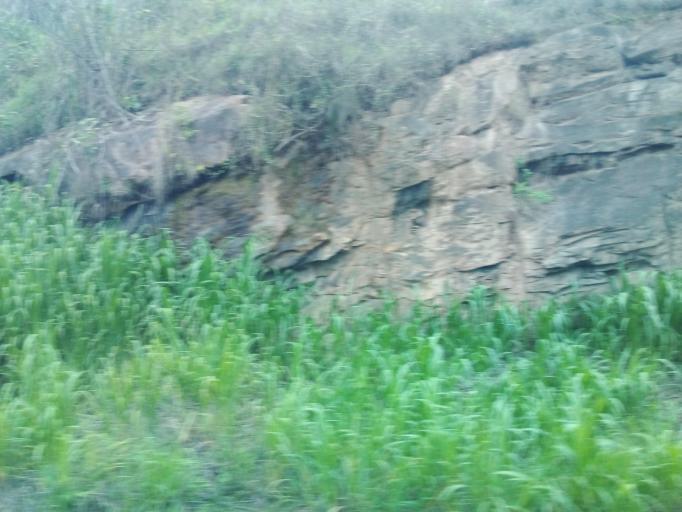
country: BR
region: Minas Gerais
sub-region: Nova Era
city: Nova Era
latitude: -19.7298
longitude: -43.0070
